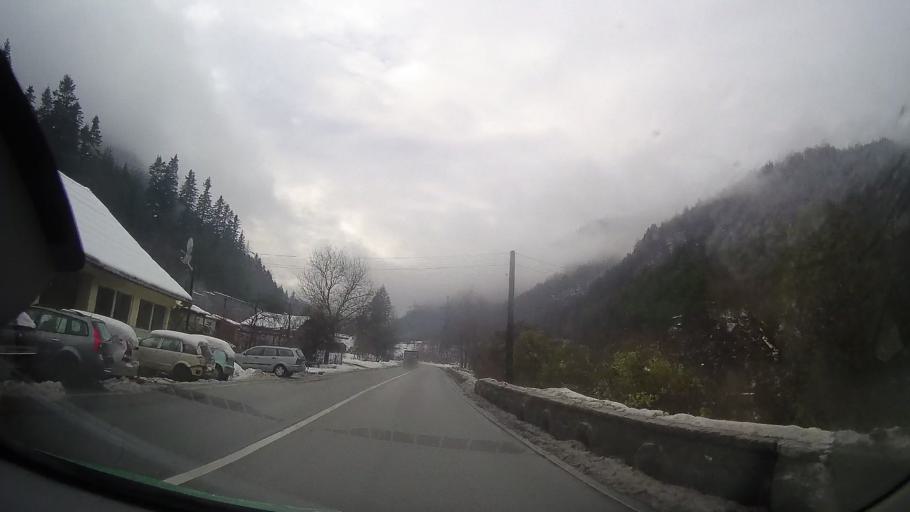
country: RO
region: Neamt
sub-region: Comuna Bicaz
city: Bicaz
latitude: 46.9004
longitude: 26.0666
